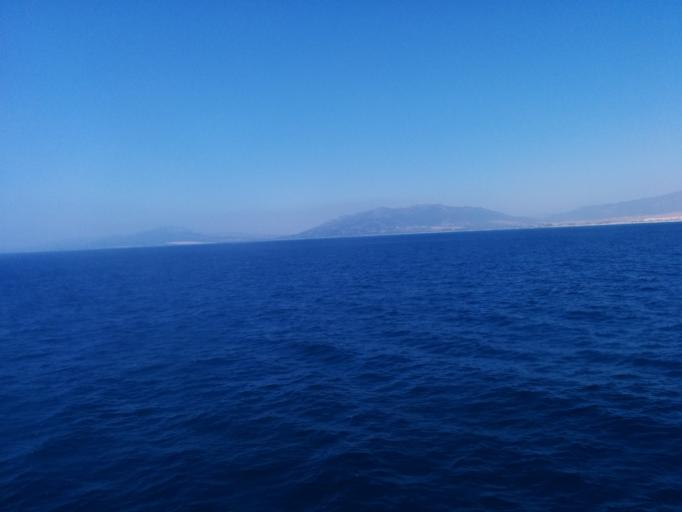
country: ES
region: Andalusia
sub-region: Provincia de Cadiz
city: Tarifa
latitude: 35.9943
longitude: -5.6138
